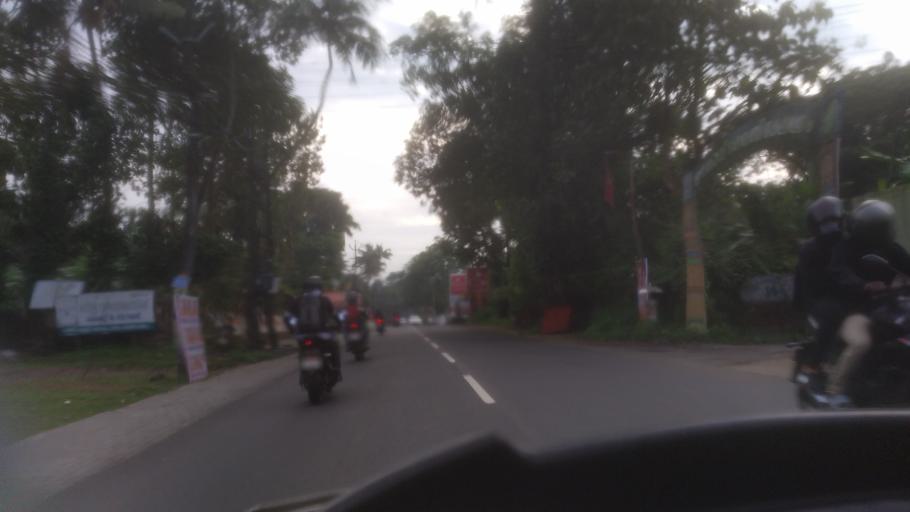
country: IN
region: Kerala
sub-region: Ernakulam
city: Kotamangalam
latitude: 10.0585
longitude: 76.6457
